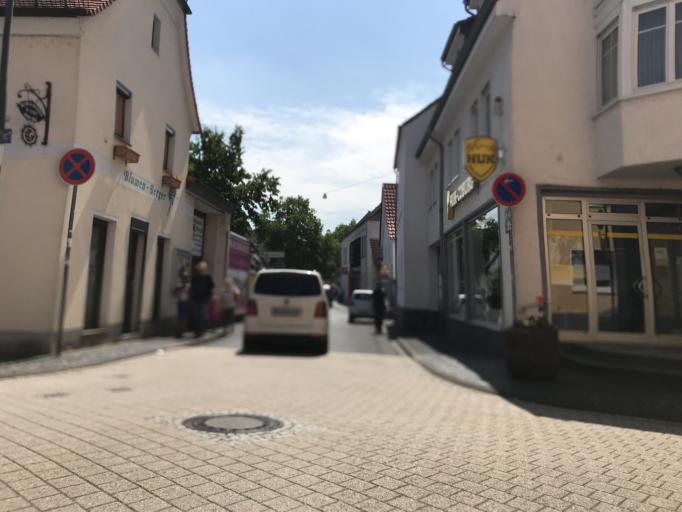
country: DE
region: Hesse
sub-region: Regierungsbezirk Darmstadt
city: Walluf
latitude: 50.0735
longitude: 8.1934
